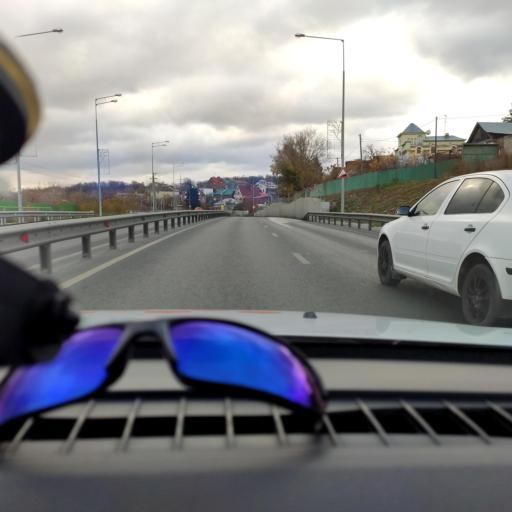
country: RU
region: Samara
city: Volzhskiy
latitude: 53.3682
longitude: 50.1931
